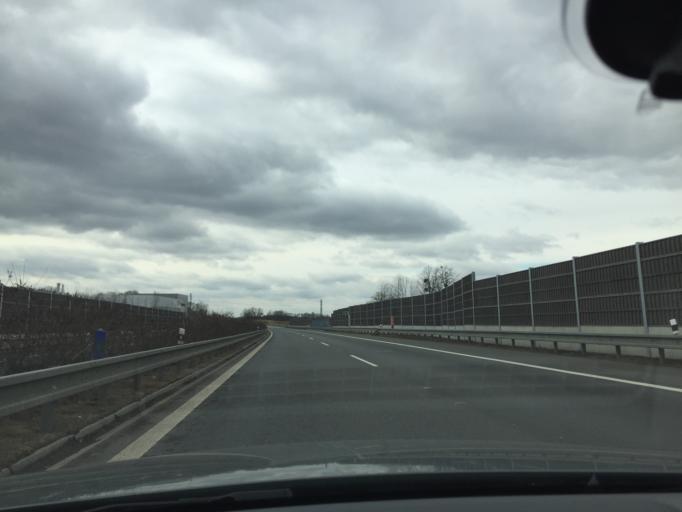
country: CZ
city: Staric
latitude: 49.6629
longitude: 18.2744
